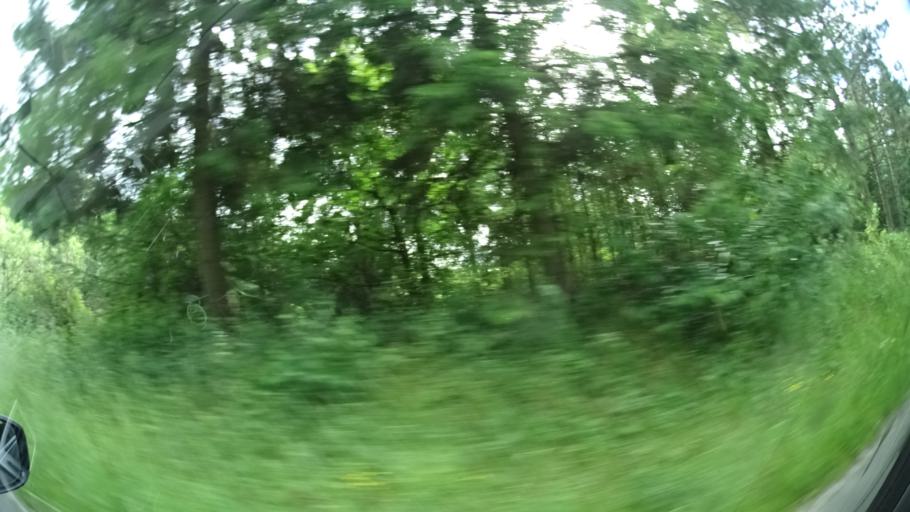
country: DK
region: Central Jutland
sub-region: Norddjurs Kommune
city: Grenaa
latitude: 56.5189
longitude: 10.7258
